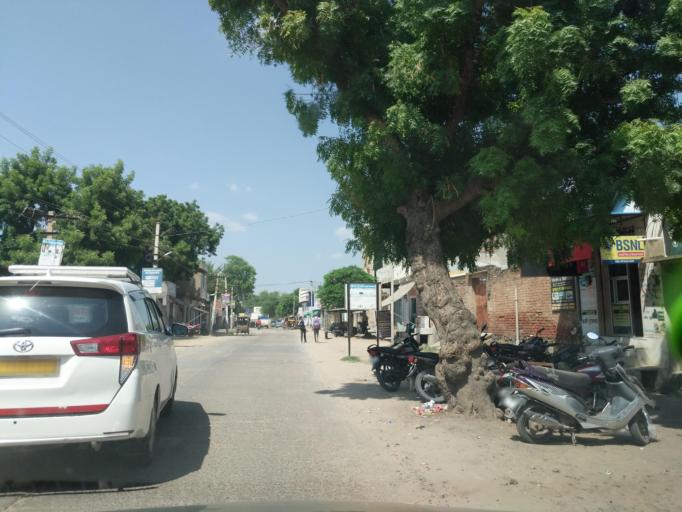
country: IN
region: Rajasthan
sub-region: Jhunjhunun
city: Jhunjhunun
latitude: 28.1353
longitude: 75.3921
